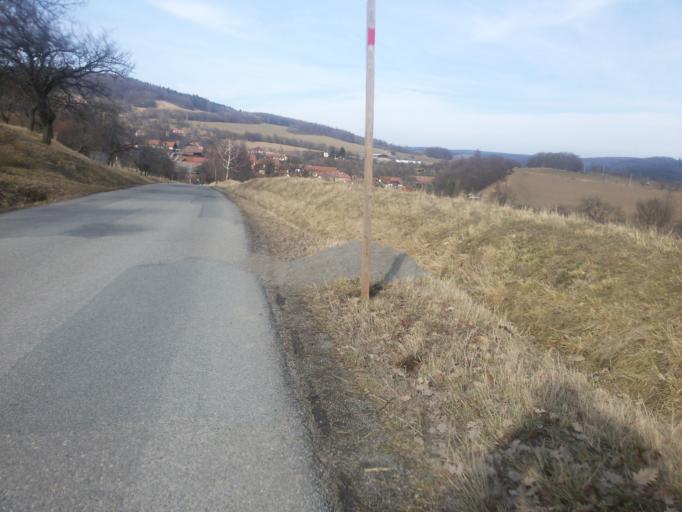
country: CZ
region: South Moravian
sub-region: Okres Brno-Venkov
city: Lomnice
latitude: 49.4286
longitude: 16.4128
